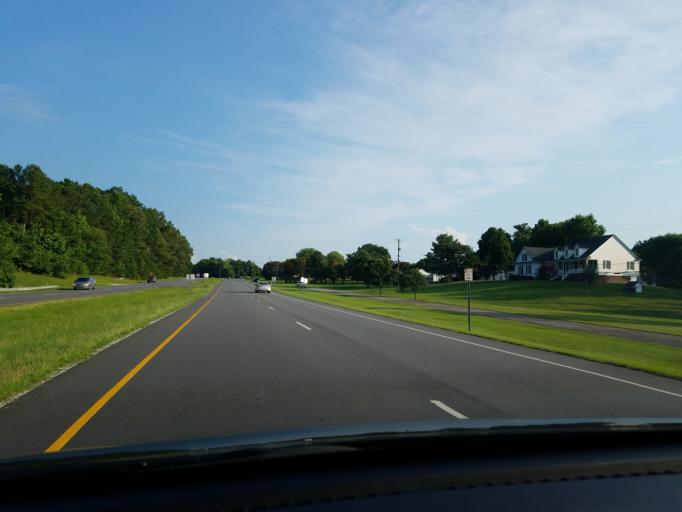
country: US
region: North Carolina
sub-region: Durham County
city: Gorman
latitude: 36.1383
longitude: -78.9057
